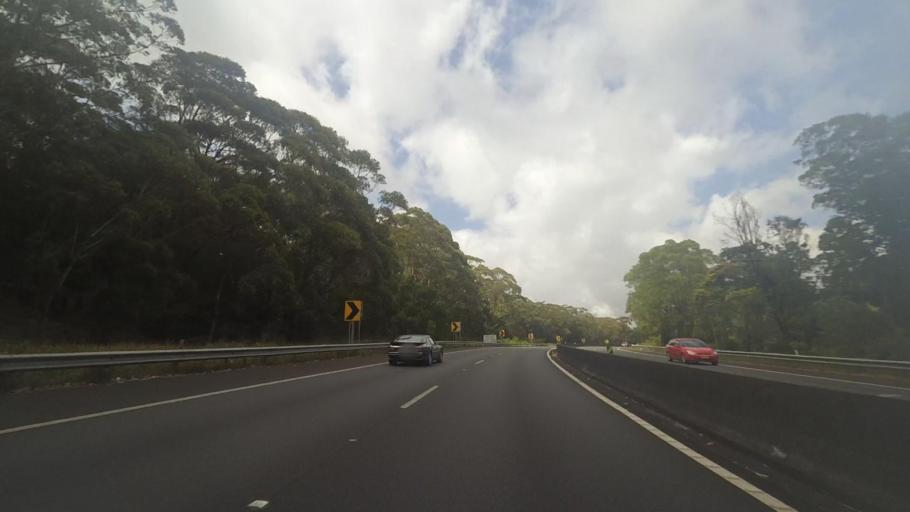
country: AU
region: New South Wales
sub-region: Wollongong
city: Bulli
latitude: -34.3448
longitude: 150.8761
